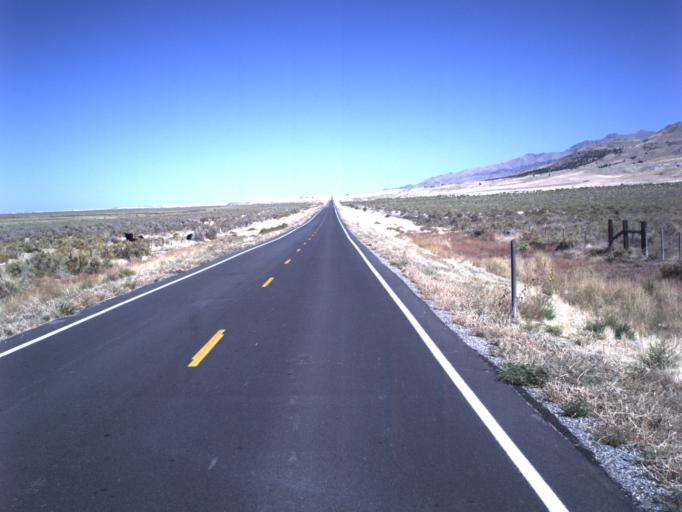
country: US
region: Utah
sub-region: Tooele County
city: Grantsville
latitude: 40.5440
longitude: -112.7437
